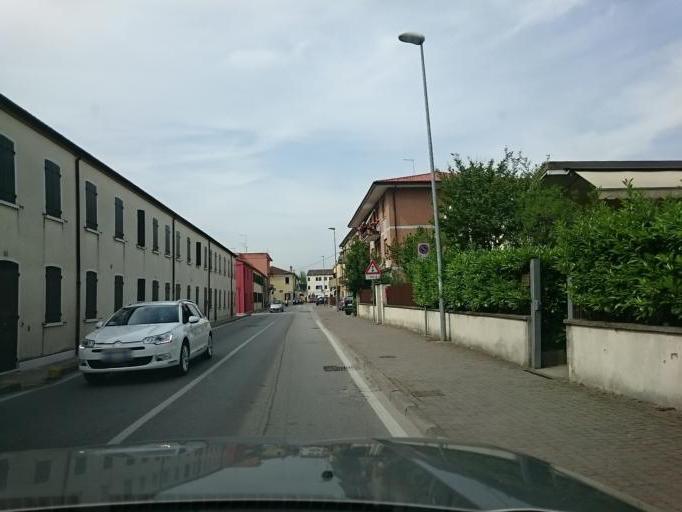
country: IT
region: Veneto
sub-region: Provincia di Venezia
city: Dolo
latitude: 45.4232
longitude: 12.0775
